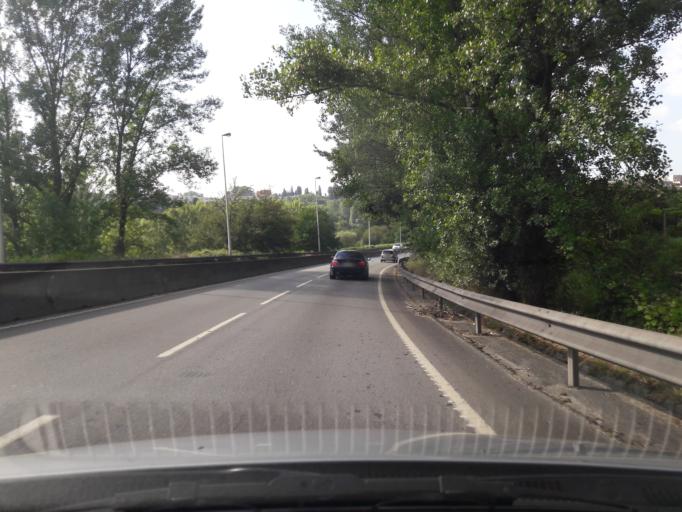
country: PT
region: Braga
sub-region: Guimaraes
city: Urgeses
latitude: 41.4365
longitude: -8.3043
